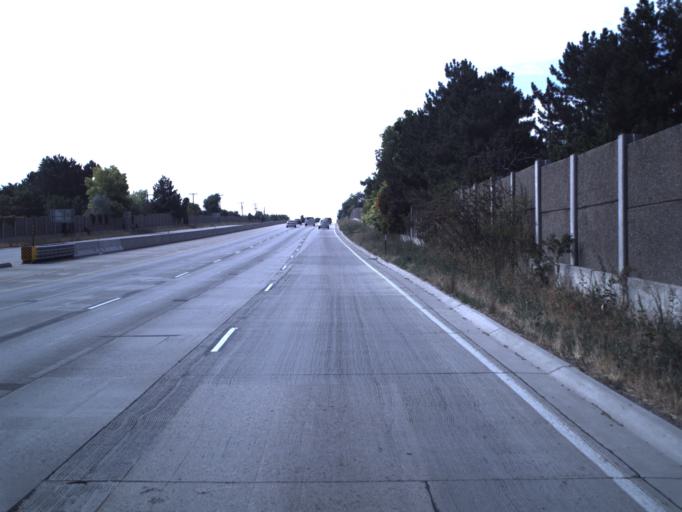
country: US
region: Utah
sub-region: Salt Lake County
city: West Valley City
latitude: 40.6789
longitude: -111.9818
